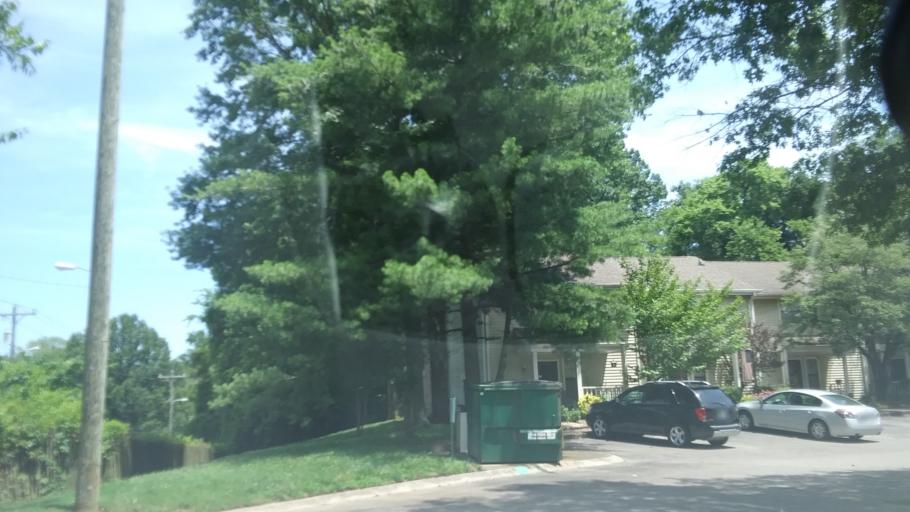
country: US
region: Tennessee
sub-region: Rutherford County
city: La Vergne
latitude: 36.0964
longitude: -86.6388
